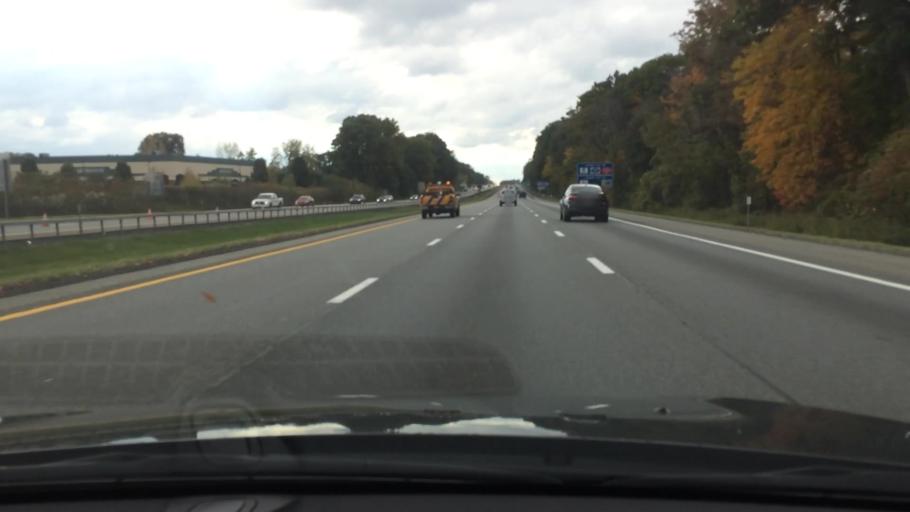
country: US
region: New York
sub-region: Saratoga County
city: Country Knolls
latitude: 42.8748
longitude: -73.7775
